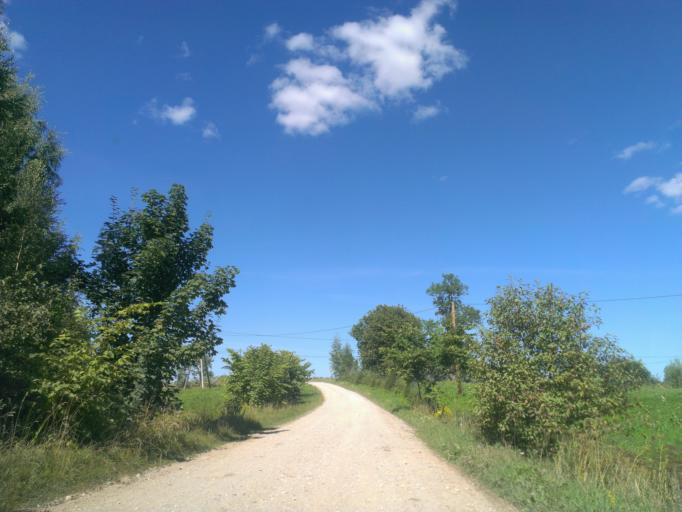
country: LV
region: Malpils
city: Malpils
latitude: 57.0149
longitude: 24.9901
